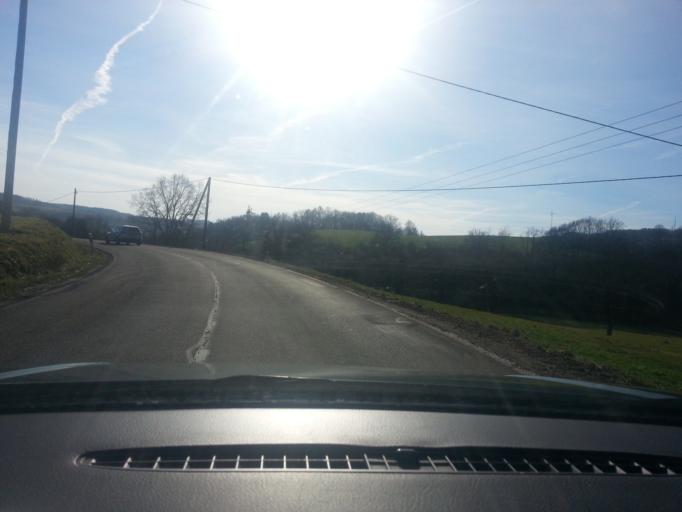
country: DE
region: Rheinland-Pfalz
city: Selchenbach
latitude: 49.4865
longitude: 7.2547
